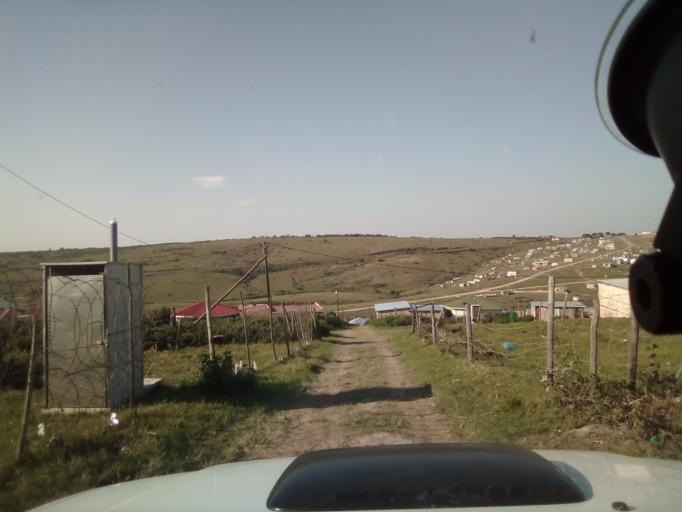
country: ZA
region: Eastern Cape
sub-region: Buffalo City Metropolitan Municipality
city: East London
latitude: -32.8461
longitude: 27.9891
